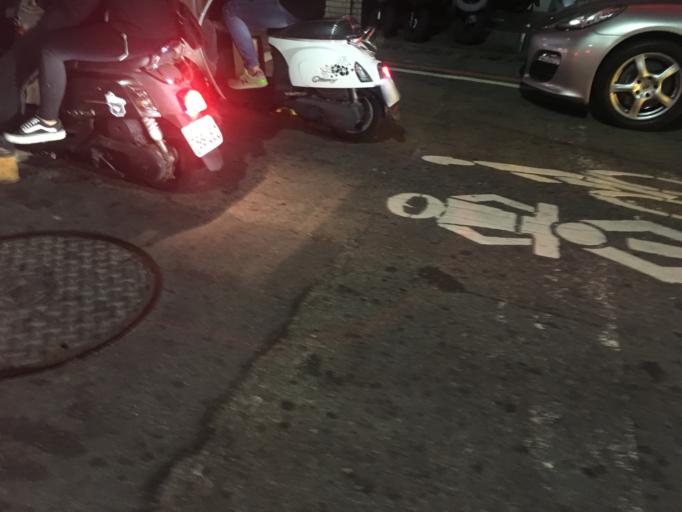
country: TW
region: Taiwan
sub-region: Hsinchu
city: Hsinchu
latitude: 24.8121
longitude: 120.9646
